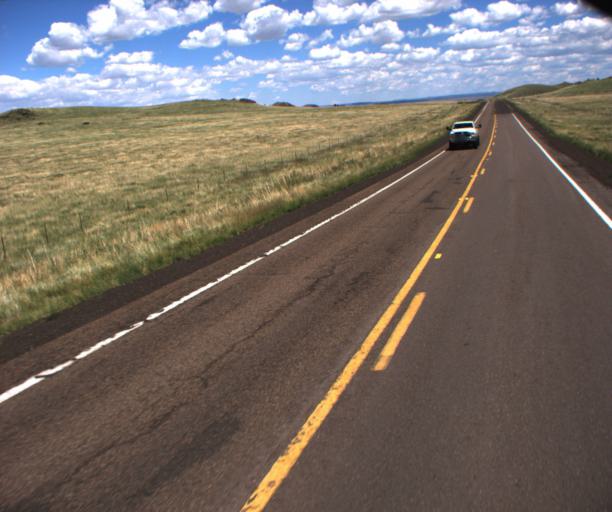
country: US
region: Arizona
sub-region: Apache County
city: Springerville
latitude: 34.2130
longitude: -109.4481
